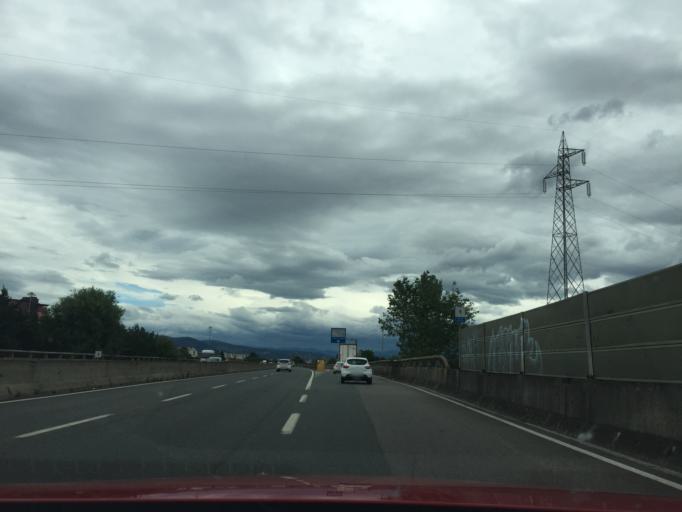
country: IT
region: Tuscany
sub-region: Province of Florence
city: Scandicci
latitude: 43.7703
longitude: 11.1829
